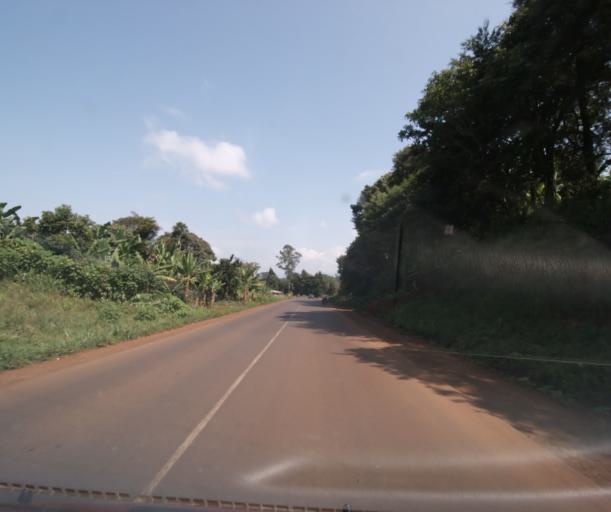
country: CM
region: West
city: Bansoa
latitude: 5.4881
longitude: 10.2664
